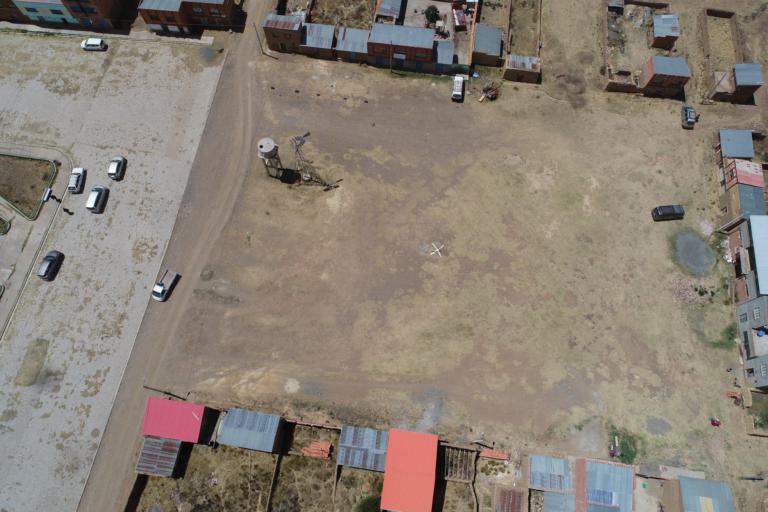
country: BO
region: La Paz
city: Achacachi
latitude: -15.9119
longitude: -68.8863
